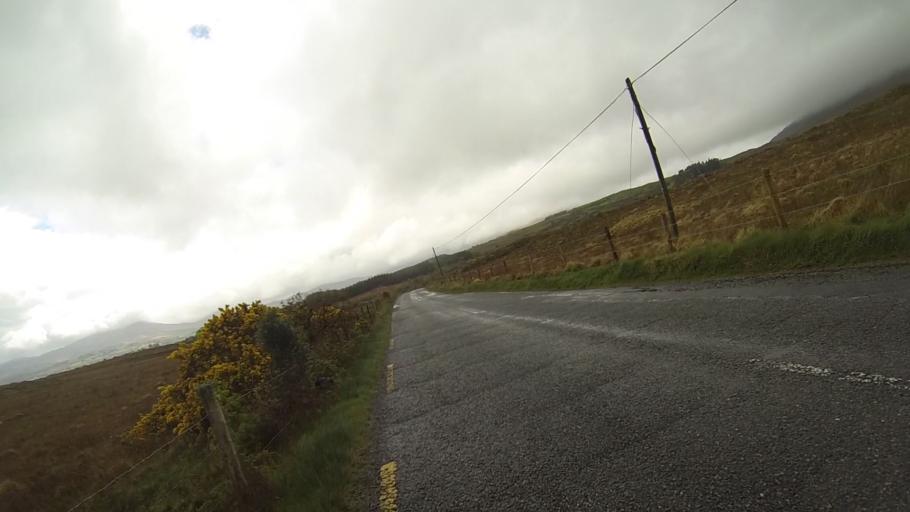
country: IE
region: Munster
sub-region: Ciarrai
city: Kenmare
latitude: 51.9064
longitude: -9.7344
